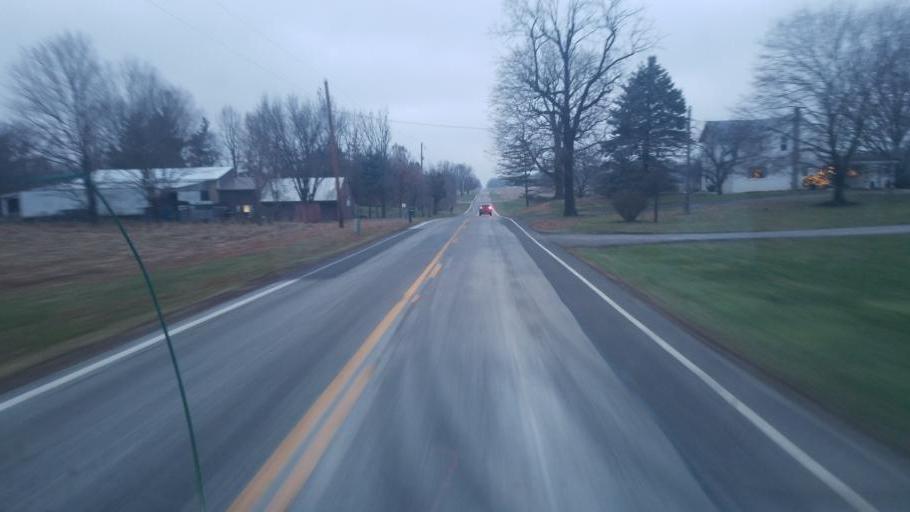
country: US
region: Ohio
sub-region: Wyandot County
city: Upper Sandusky
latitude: 40.8794
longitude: -83.1316
